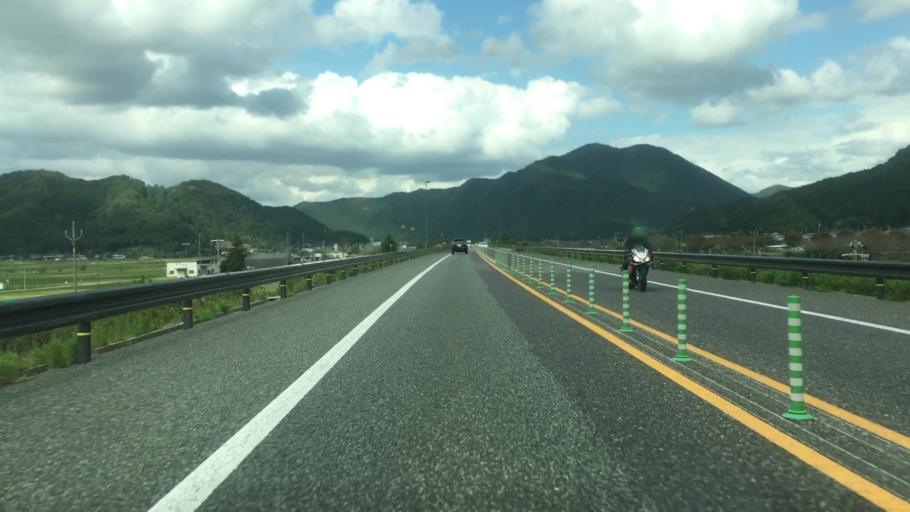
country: JP
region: Kyoto
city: Fukuchiyama
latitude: 35.2114
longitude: 135.0364
